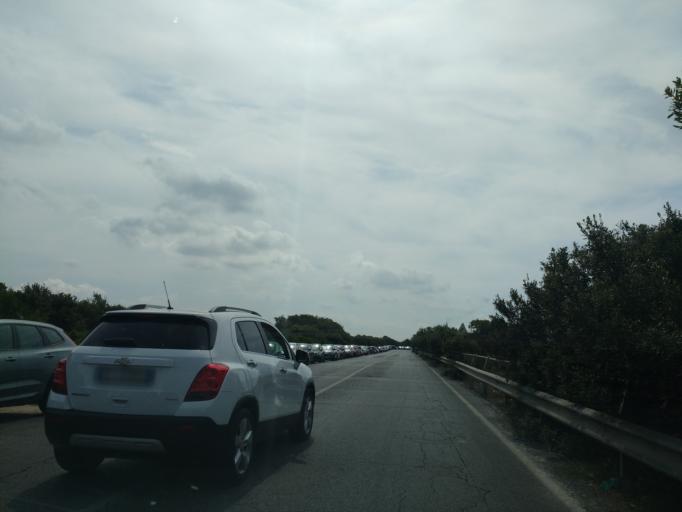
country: IT
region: Latium
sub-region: Citta metropolitana di Roma Capitale
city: Torvaianica
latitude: 41.6644
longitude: 12.4061
